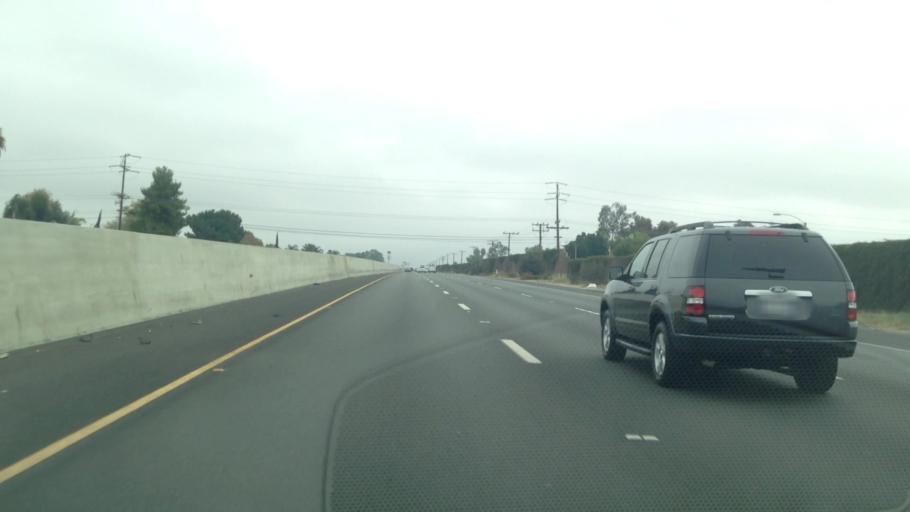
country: US
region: California
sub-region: Riverside County
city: Moreno Valley
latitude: 33.9392
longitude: -117.2193
